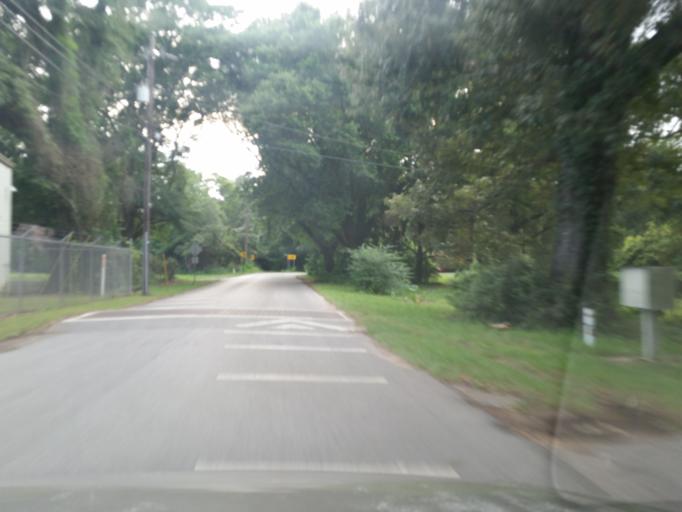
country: US
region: Florida
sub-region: Escambia County
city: Ferry Pass
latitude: 30.5053
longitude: -87.2265
